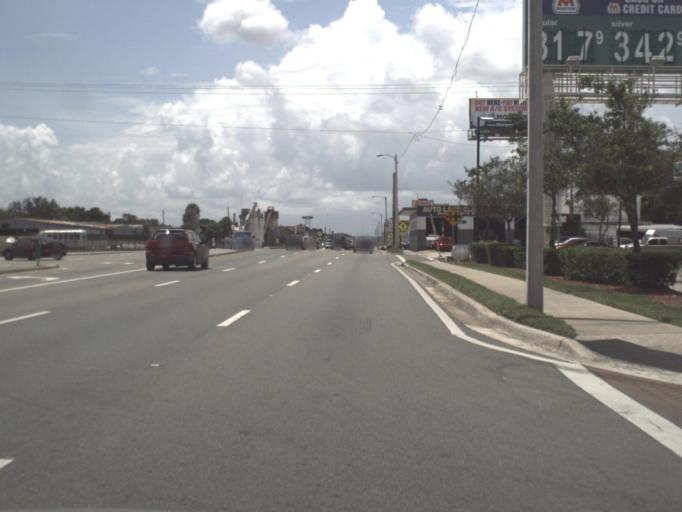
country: US
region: Florida
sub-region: Hillsborough County
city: University
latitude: 28.0329
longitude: -82.4448
